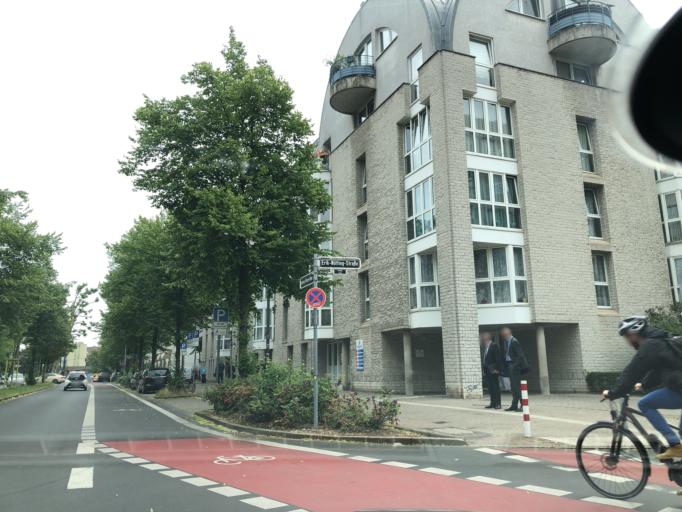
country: DE
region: North Rhine-Westphalia
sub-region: Regierungsbezirk Dusseldorf
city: Dusseldorf
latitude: 51.2198
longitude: 6.7973
